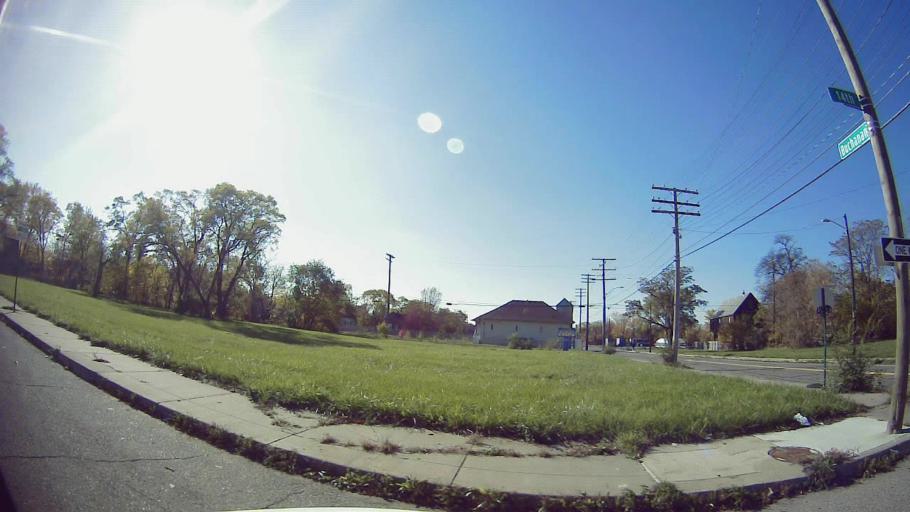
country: US
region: Michigan
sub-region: Wayne County
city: Detroit
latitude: 42.3450
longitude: -83.0843
